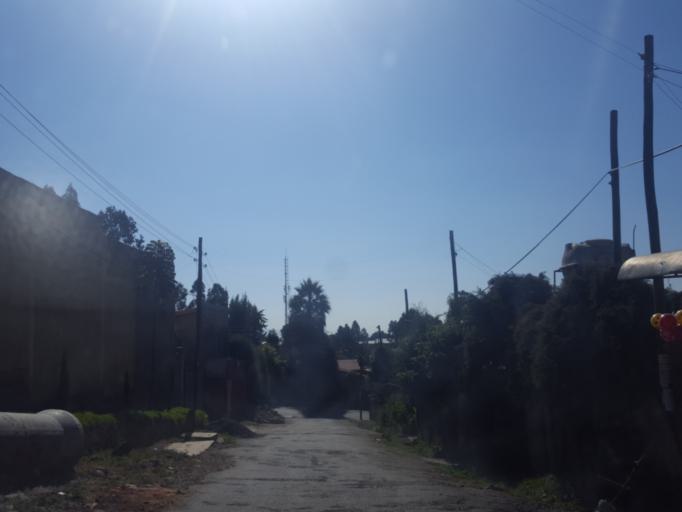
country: ET
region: Adis Abeba
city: Addis Ababa
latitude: 9.0568
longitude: 38.7369
